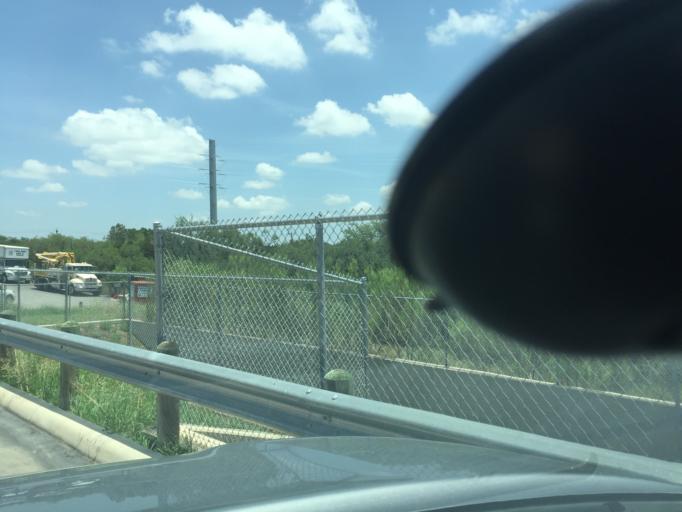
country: US
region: Texas
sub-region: Bexar County
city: Timberwood Park
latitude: 29.6915
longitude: -98.4513
